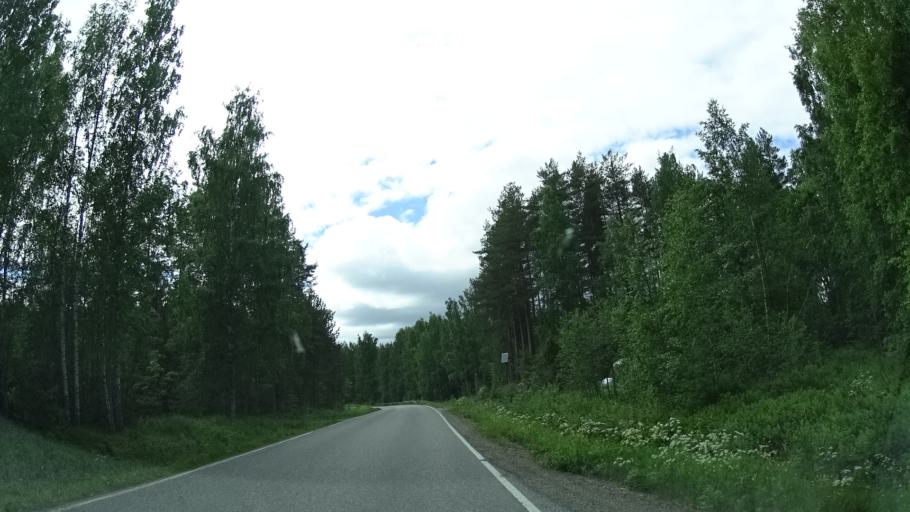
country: FI
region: Central Finland
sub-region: Joutsa
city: Luhanka
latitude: 61.7603
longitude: 25.5819
